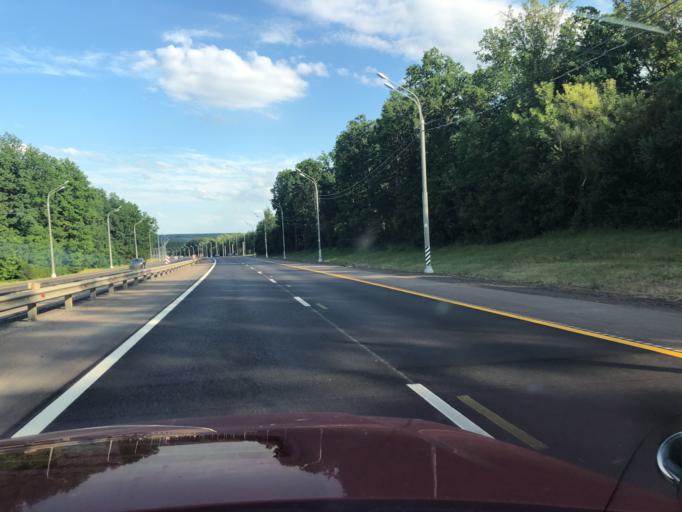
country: RU
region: Lipetsk
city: Zadonsk
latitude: 52.3847
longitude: 38.8699
